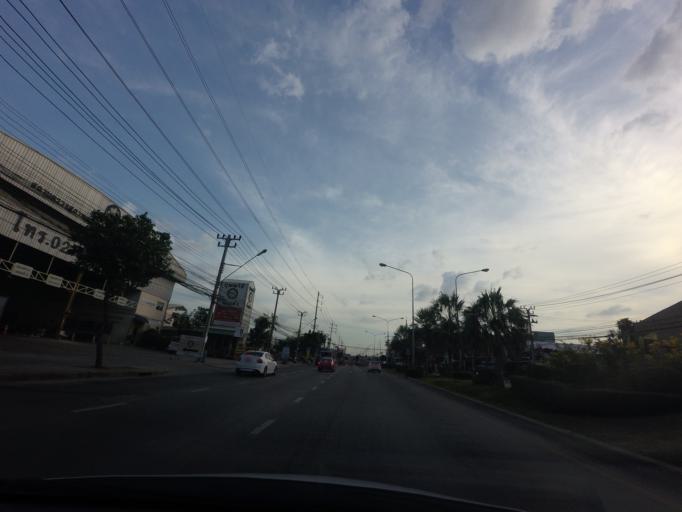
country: TH
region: Bangkok
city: Bang Khun Thian
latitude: 13.6310
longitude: 100.4340
